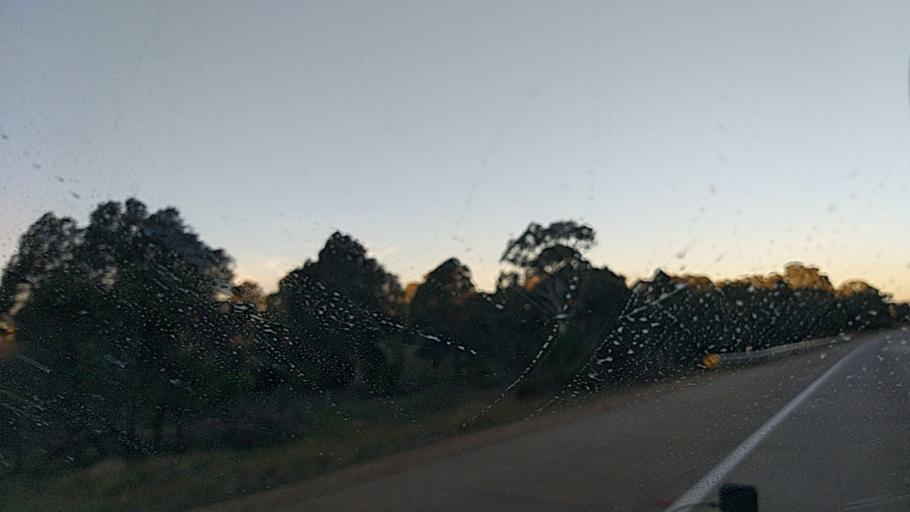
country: AU
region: New South Wales
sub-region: Goulburn Mulwaree
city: Goulburn
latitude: -34.7743
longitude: 149.7526
